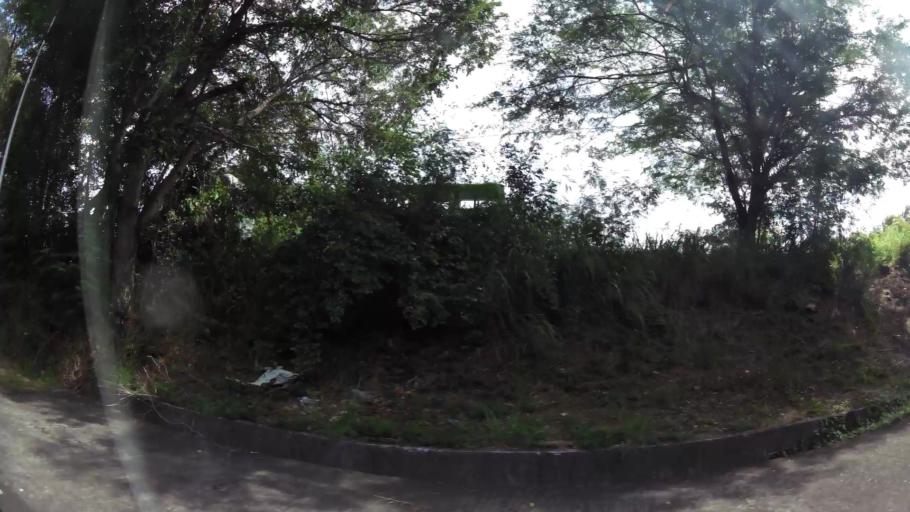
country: GP
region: Guadeloupe
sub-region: Guadeloupe
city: Basse-Terre
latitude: 16.0046
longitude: -61.7199
